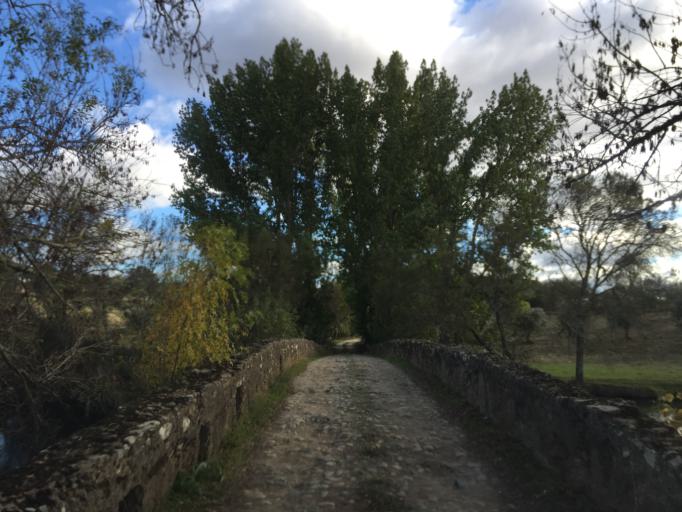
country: PT
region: Portalegre
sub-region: Alter do Chao
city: Alter do Chao
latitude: 39.2716
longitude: -7.6410
